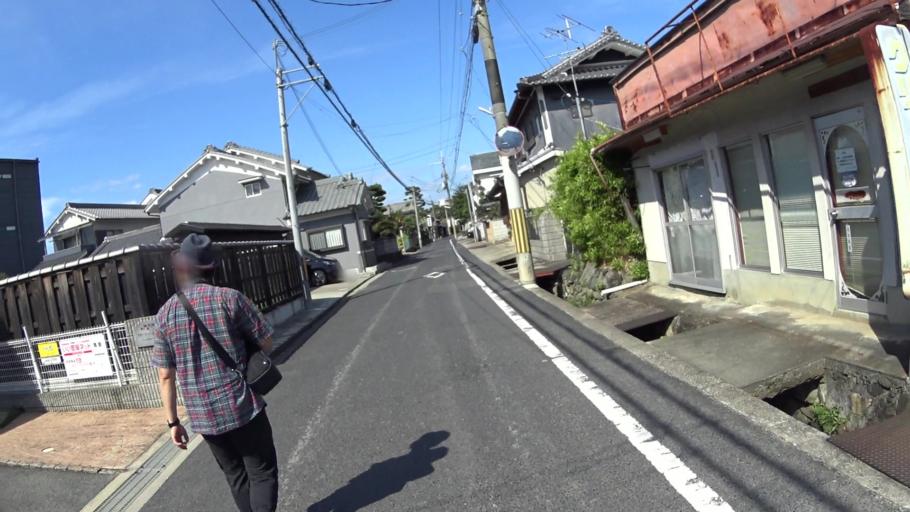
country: JP
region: Nara
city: Sakurai
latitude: 34.5324
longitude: 135.8416
